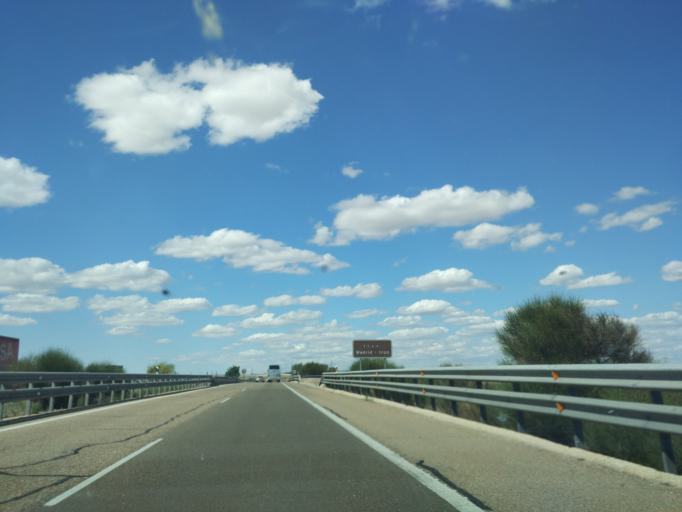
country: ES
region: Castille and Leon
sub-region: Provincia de Valladolid
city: Medina del Campo
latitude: 41.2961
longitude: -4.9013
